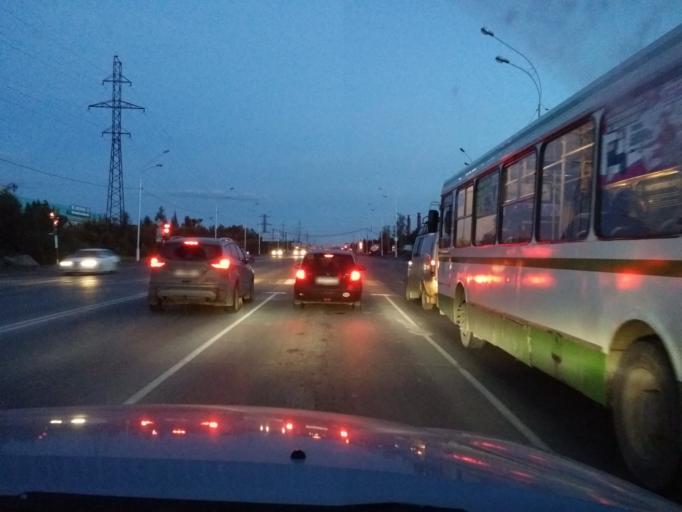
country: RU
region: Khanty-Mansiyskiy Avtonomnyy Okrug
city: Nizhnevartovsk
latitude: 60.9558
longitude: 76.5300
